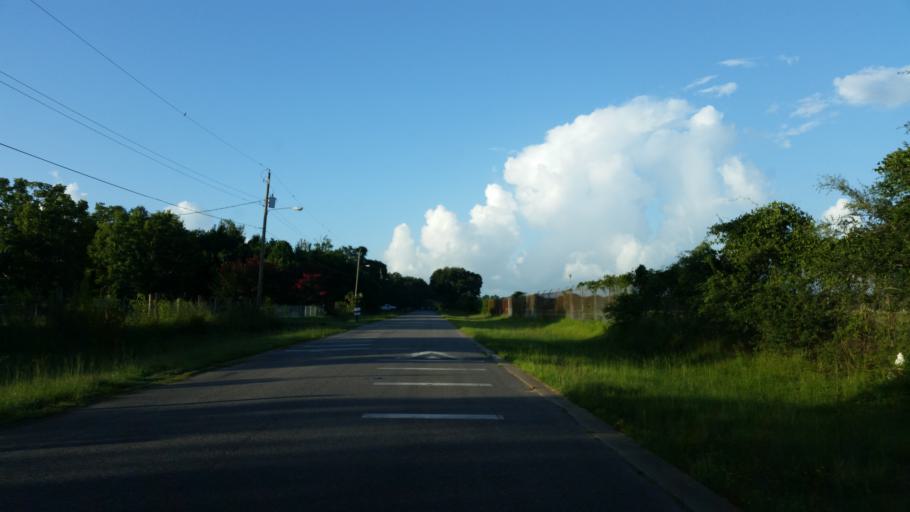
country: US
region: Florida
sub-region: Escambia County
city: Bellview
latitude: 30.4682
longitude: -87.3325
